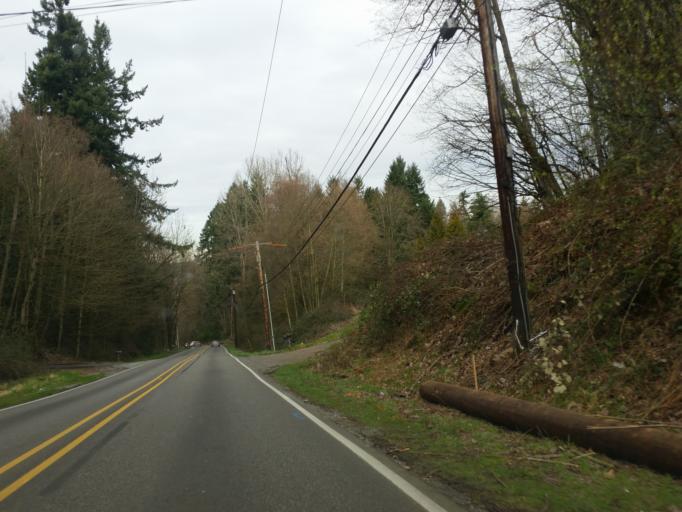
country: US
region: Washington
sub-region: Pierce County
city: Alderton
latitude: 47.1733
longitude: -122.2538
